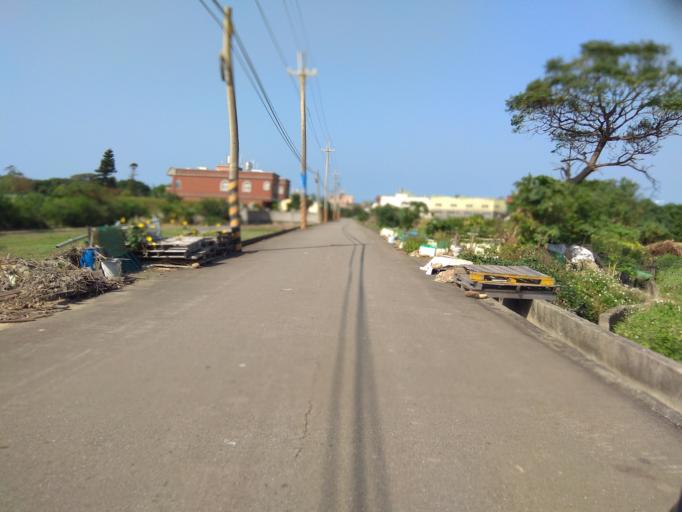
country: TW
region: Taiwan
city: Taoyuan City
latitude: 25.0485
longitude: 121.2159
